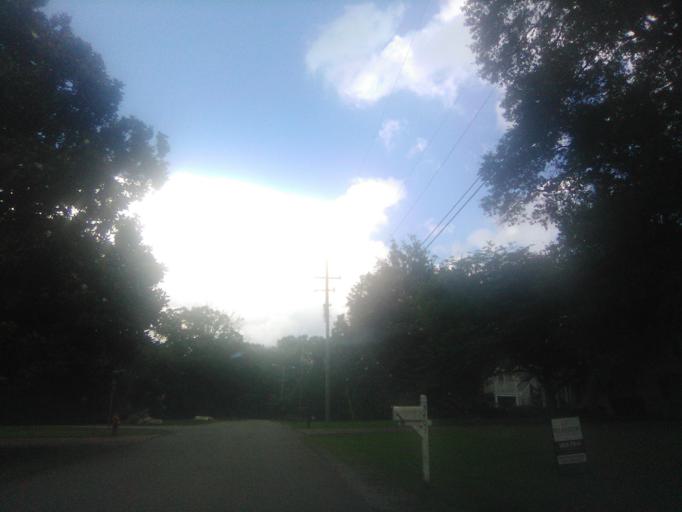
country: US
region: Tennessee
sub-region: Davidson County
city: Belle Meade
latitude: 36.1141
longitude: -86.8293
